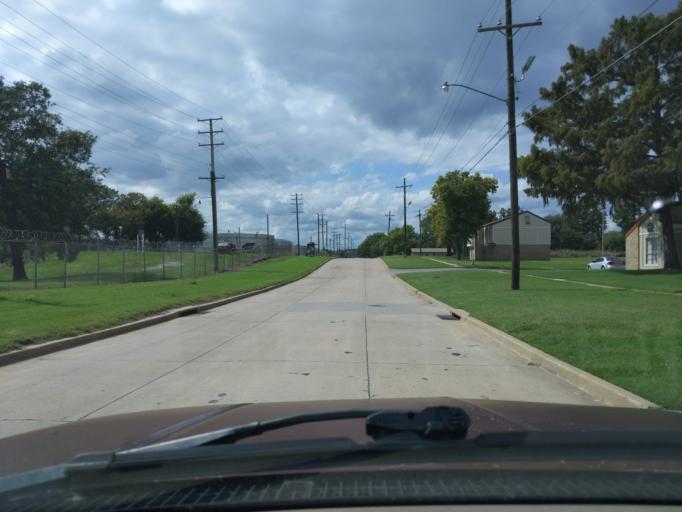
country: US
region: Oklahoma
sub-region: Tulsa County
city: Tulsa
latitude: 36.1263
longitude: -96.0005
